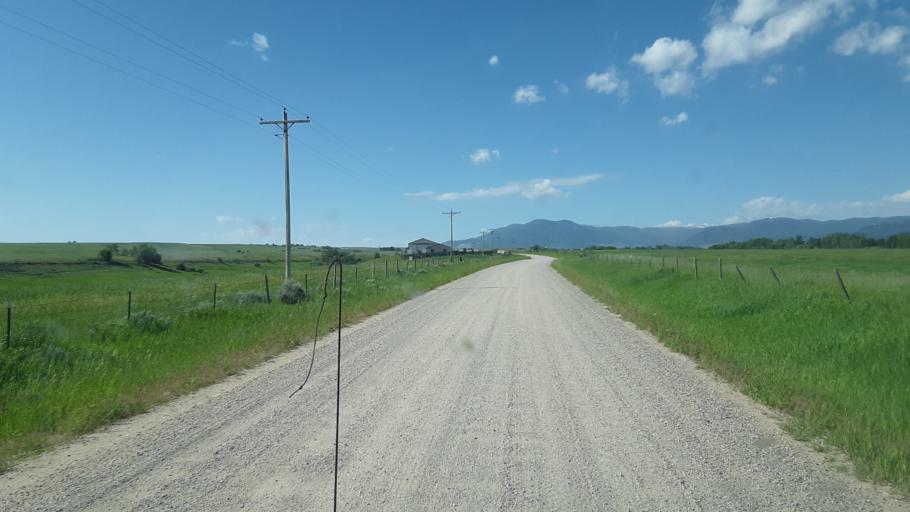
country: US
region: Montana
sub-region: Carbon County
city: Red Lodge
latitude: 45.2886
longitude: -109.1886
